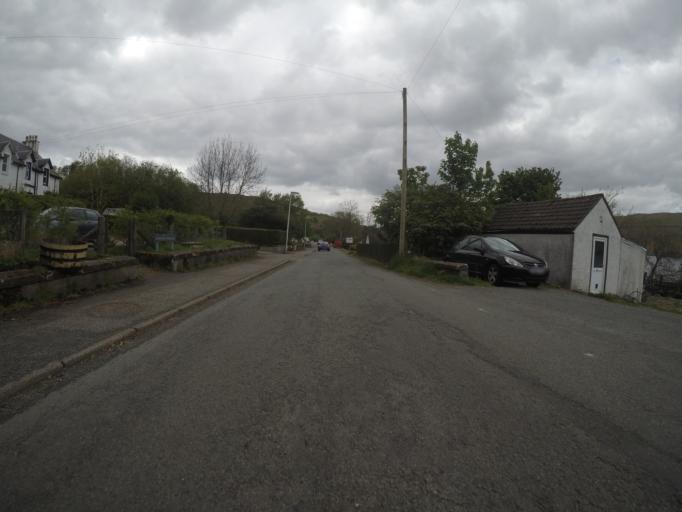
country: GB
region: Scotland
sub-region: Highland
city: Isle of Skye
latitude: 57.3010
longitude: -6.3518
